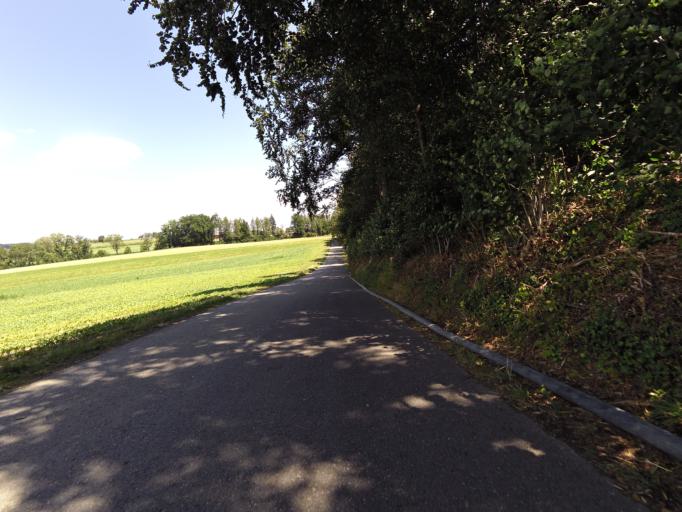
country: CH
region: Thurgau
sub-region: Weinfelden District
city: Maerstetten-Dorf
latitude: 47.6022
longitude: 9.0563
